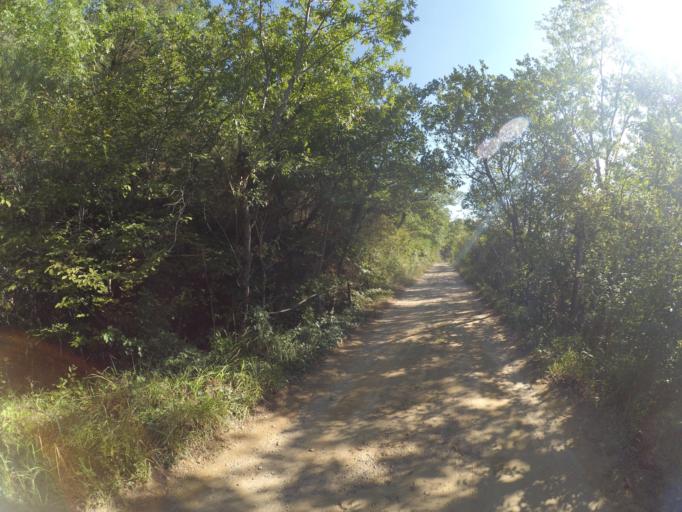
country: IT
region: Tuscany
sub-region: Province of Arezzo
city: Castiglion Fibocchi
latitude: 43.5408
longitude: 11.7696
